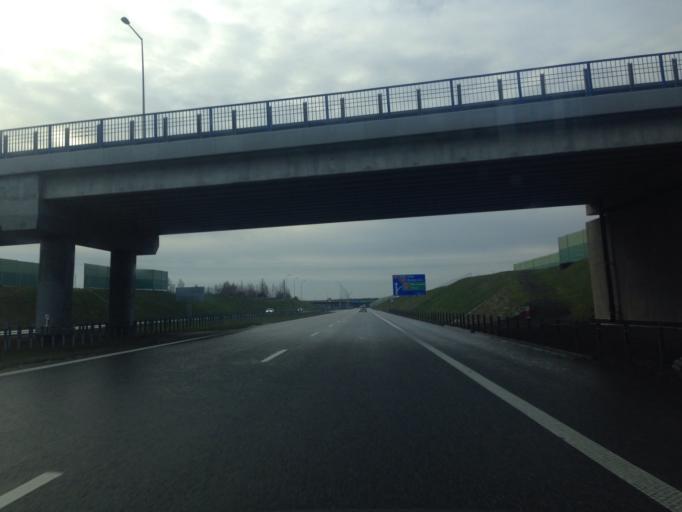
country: PL
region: Kujawsko-Pomorskie
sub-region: Powiat torunski
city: Lubicz Dolny
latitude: 53.0449
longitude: 18.7372
